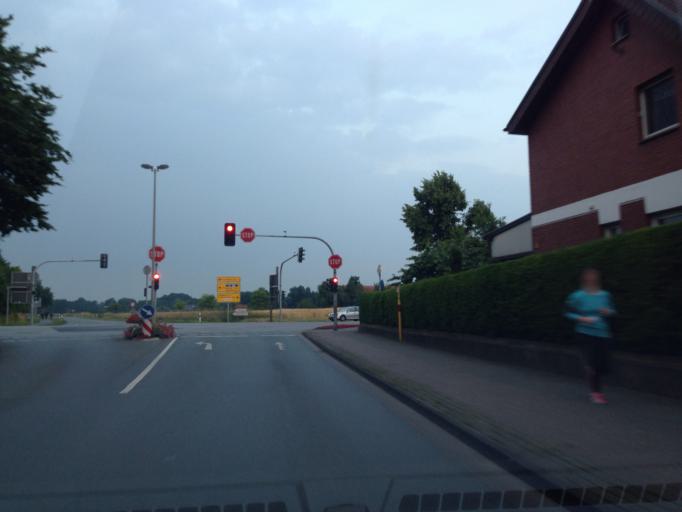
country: DE
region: North Rhine-Westphalia
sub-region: Regierungsbezirk Munster
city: Senden
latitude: 51.8572
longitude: 7.4922
